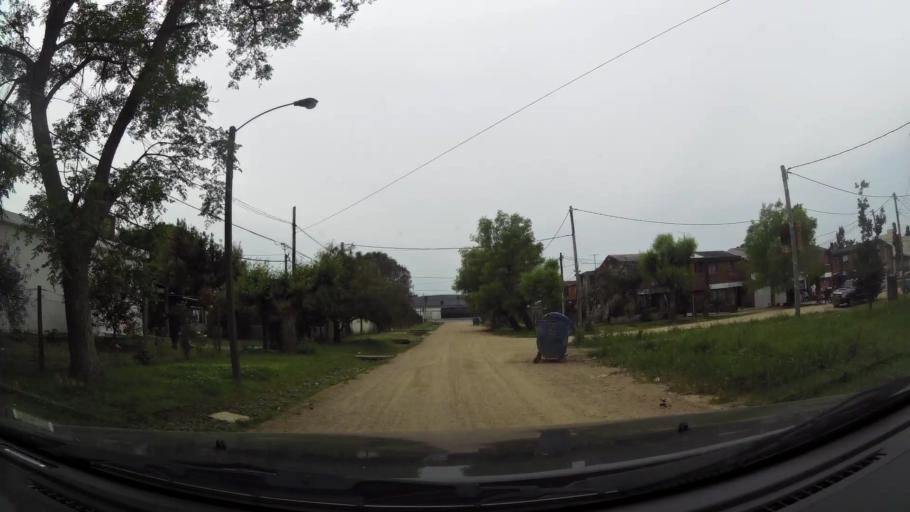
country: UY
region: Canelones
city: La Paz
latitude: -34.7505
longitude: -56.2250
